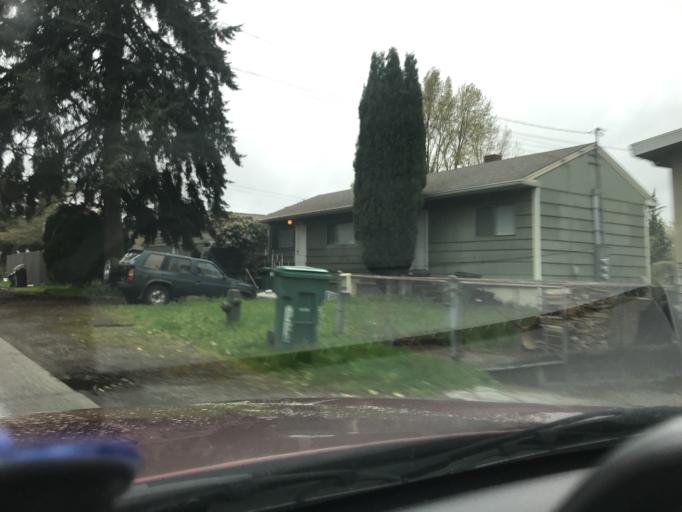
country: US
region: Washington
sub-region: King County
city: Lake Forest Park
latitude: 47.6976
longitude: -122.3005
